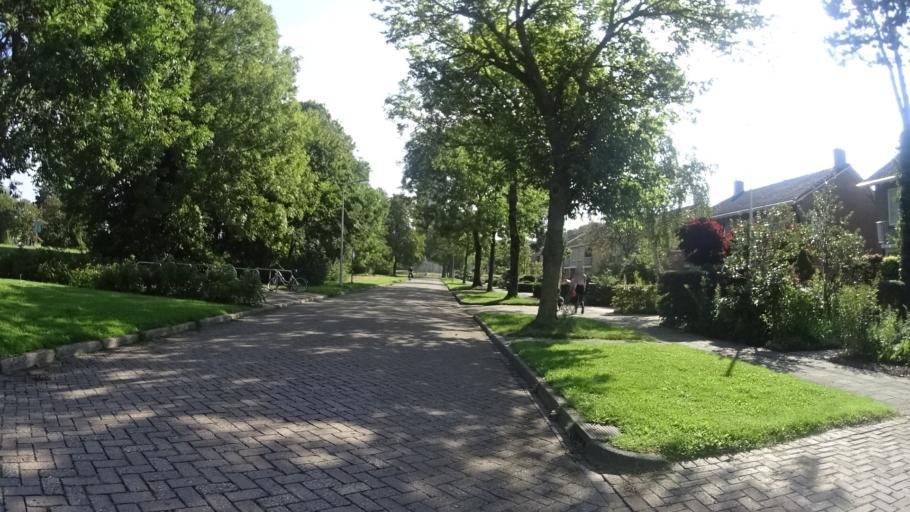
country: NL
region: Friesland
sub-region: Gemeente Franekeradeel
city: Franeker
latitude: 53.1872
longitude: 5.5554
